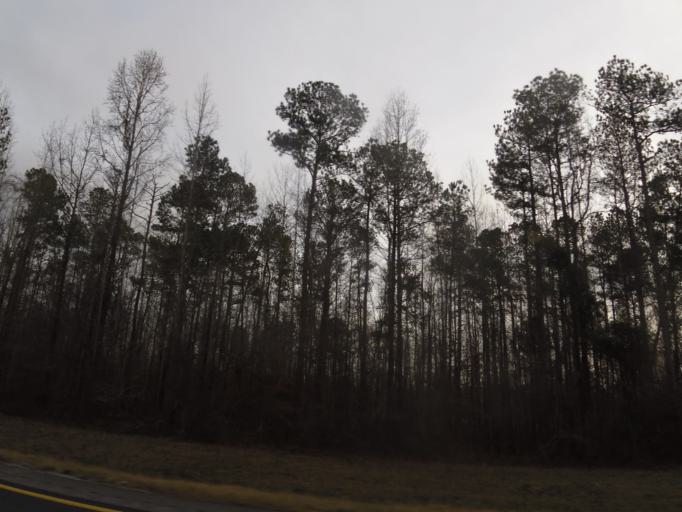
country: US
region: Alabama
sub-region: Chilton County
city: Clanton
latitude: 32.7768
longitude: -86.5702
